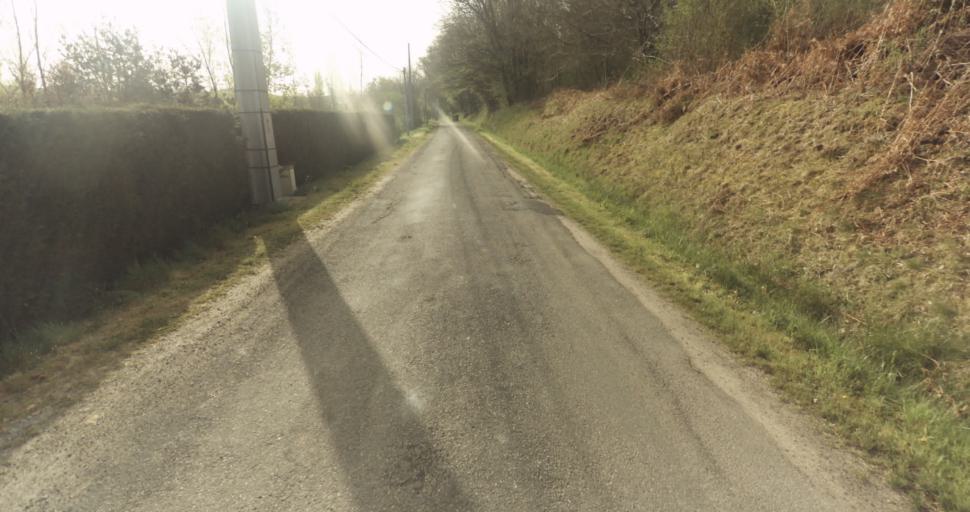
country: FR
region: Midi-Pyrenees
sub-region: Departement du Tarn-et-Garonne
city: Moissac
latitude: 44.1414
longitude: 1.0977
